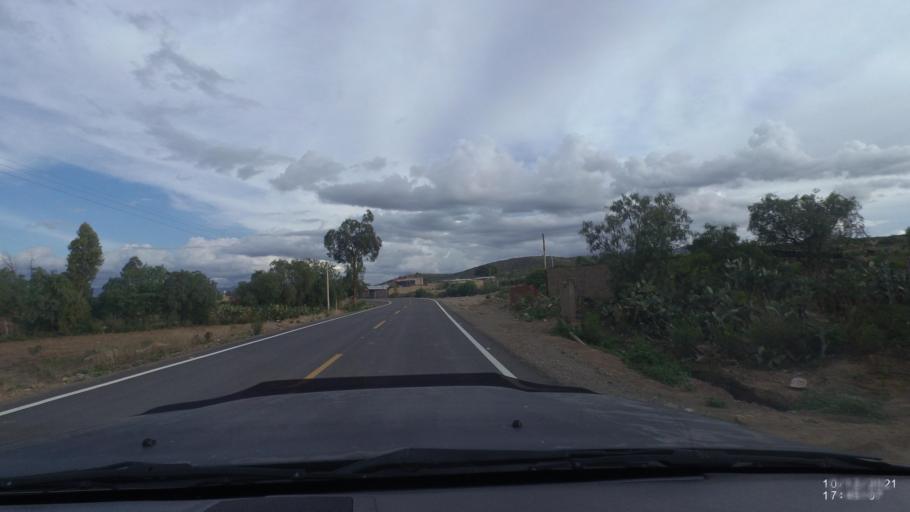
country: BO
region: Cochabamba
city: Tarata
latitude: -17.6248
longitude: -66.0060
